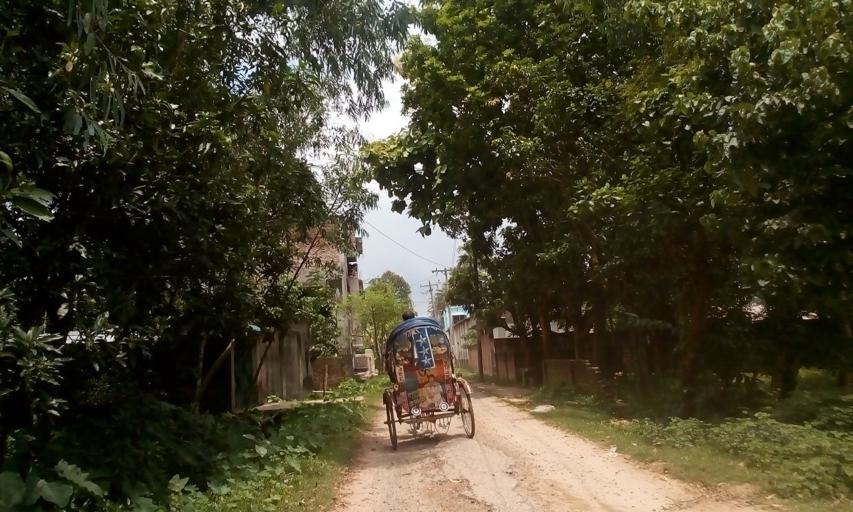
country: BD
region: Rangpur Division
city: Parbatipur
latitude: 25.3998
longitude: 88.9889
